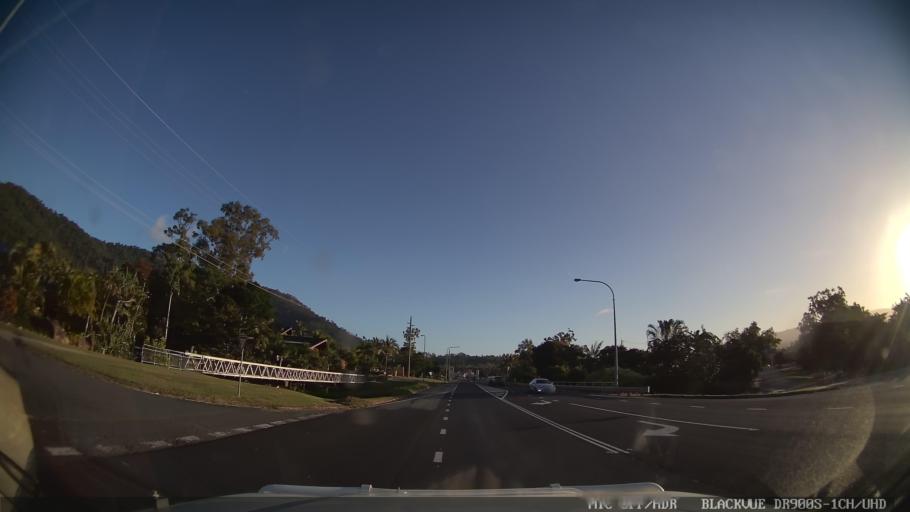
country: AU
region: Queensland
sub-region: Whitsunday
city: Proserpine
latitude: -20.2743
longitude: 148.7032
